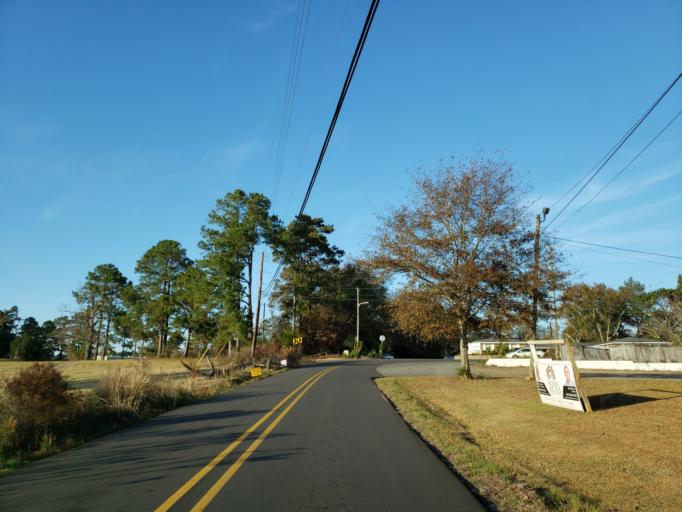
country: US
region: Mississippi
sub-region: Lamar County
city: Arnold Line
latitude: 31.3475
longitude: -89.3608
